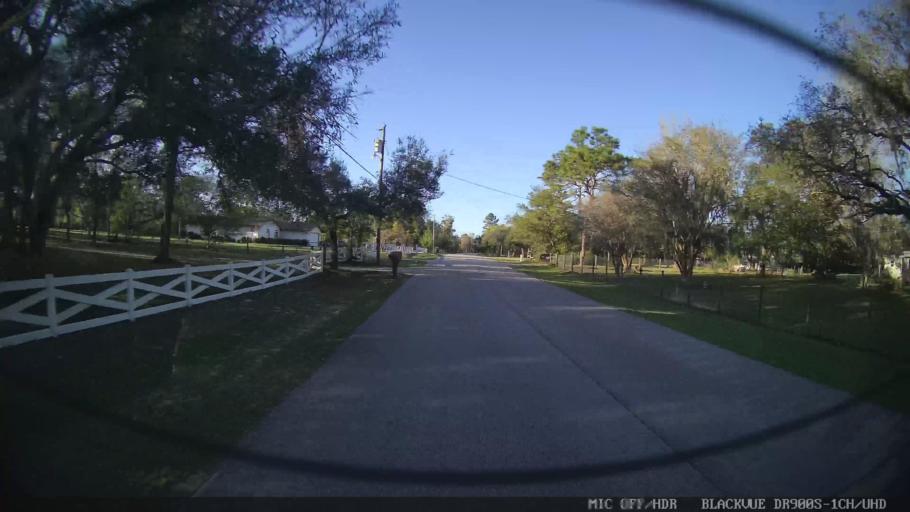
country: US
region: Florida
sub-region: Pasco County
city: Shady Hills
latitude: 28.4117
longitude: -82.5738
